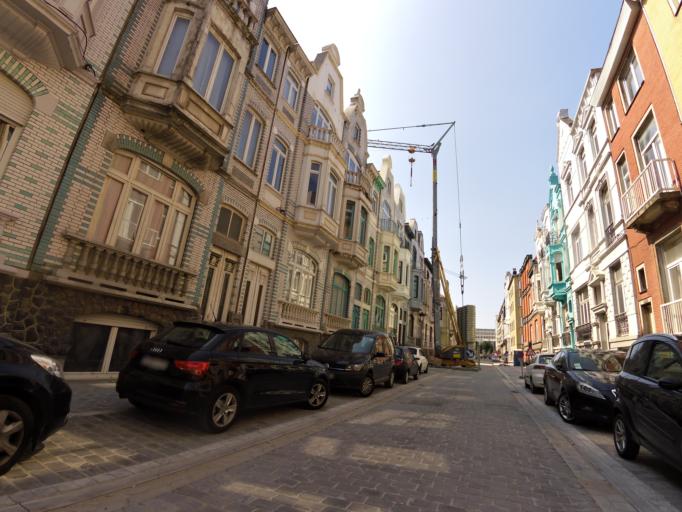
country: BE
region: Flanders
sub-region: Provincie West-Vlaanderen
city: Ostend
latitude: 51.2234
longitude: 2.9051
